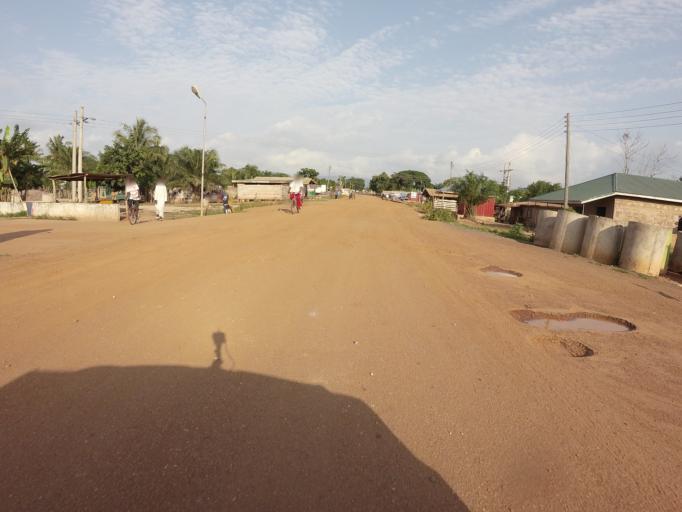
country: GH
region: Volta
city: Kpandu
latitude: 7.0026
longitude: 0.4347
